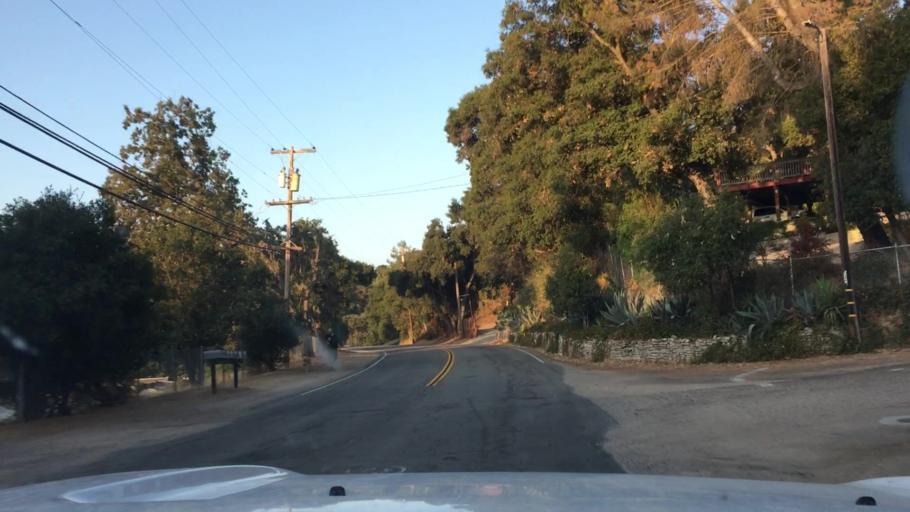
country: US
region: California
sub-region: San Luis Obispo County
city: Atascadero
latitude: 35.4854
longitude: -120.6736
